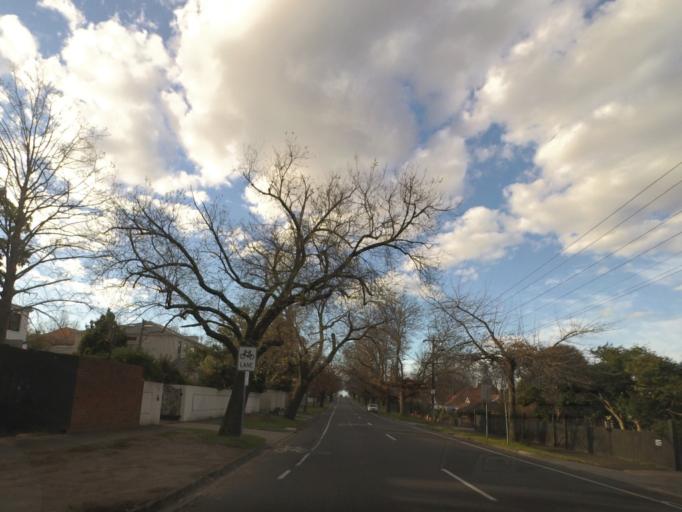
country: AU
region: Victoria
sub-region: Boroondara
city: Canterbury
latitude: -37.8180
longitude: 145.0803
